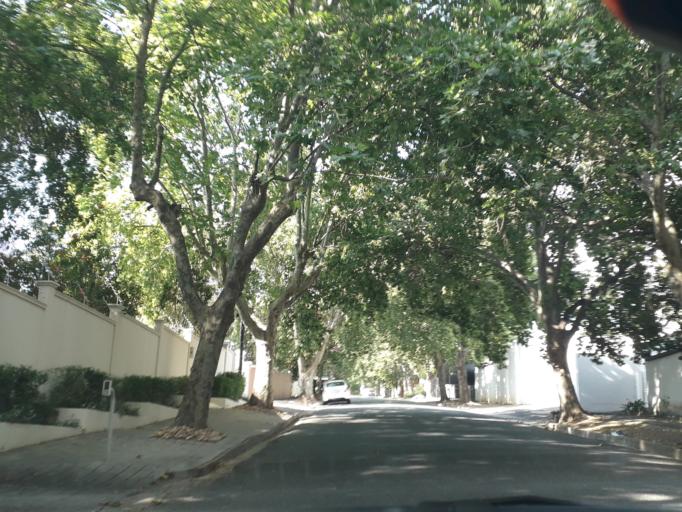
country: ZA
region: Gauteng
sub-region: City of Johannesburg Metropolitan Municipality
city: Johannesburg
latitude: -26.1481
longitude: 28.0330
